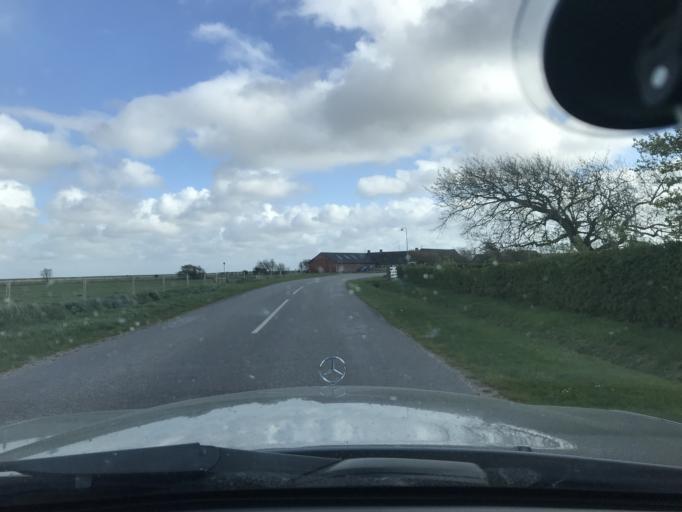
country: DE
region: Schleswig-Holstein
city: List
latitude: 55.1763
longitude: 8.5572
